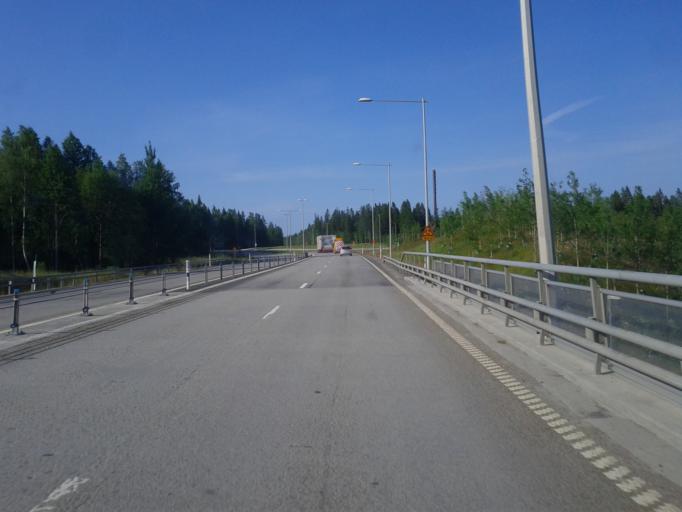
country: SE
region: Vaesterbotten
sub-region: Umea Kommun
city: Ersmark
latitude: 63.8452
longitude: 20.3405
